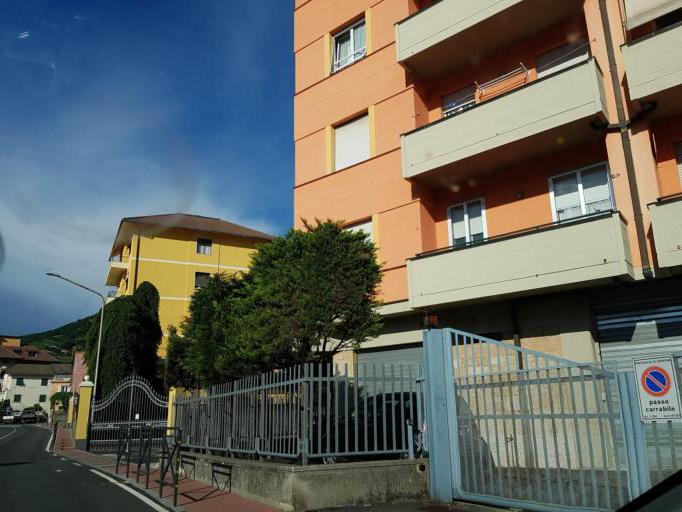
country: IT
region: Liguria
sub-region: Provincia di Genova
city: Manesseno
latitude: 44.4774
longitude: 8.9183
